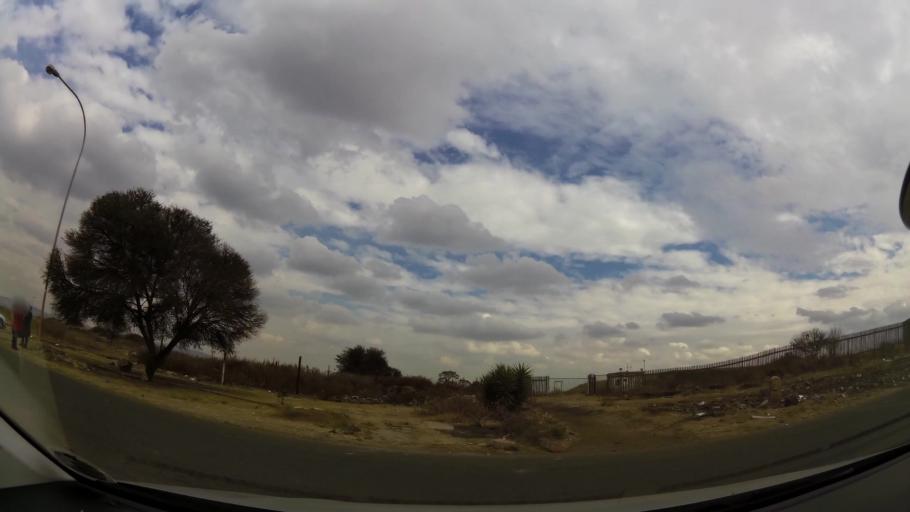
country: ZA
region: Gauteng
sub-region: City of Johannesburg Metropolitan Municipality
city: Soweto
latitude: -26.2758
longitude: 27.8556
